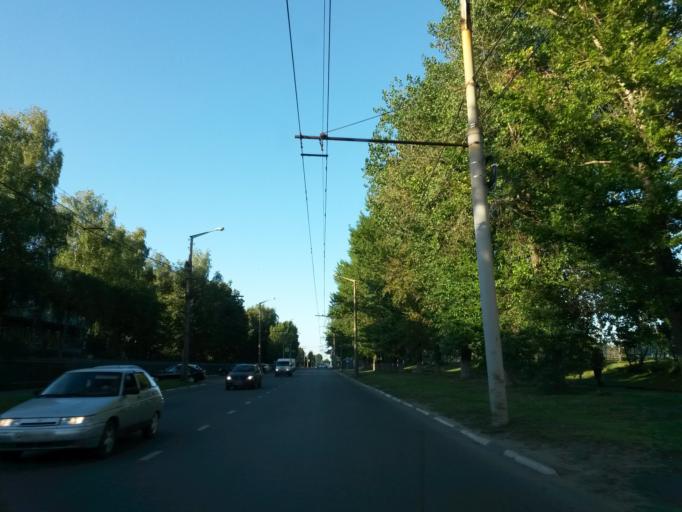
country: RU
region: Jaroslavl
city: Yaroslavl
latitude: 57.5866
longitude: 39.8429
